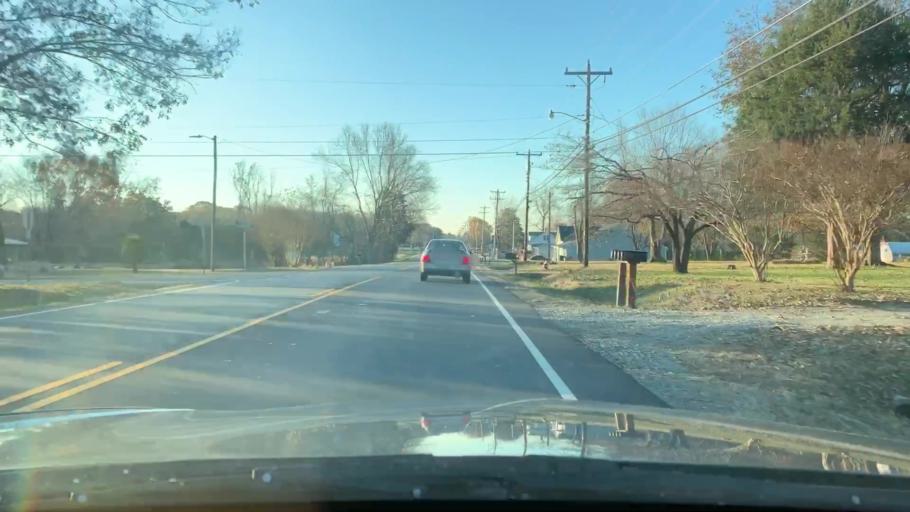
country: US
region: North Carolina
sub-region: Alamance County
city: Haw River
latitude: 36.0883
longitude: -79.3479
